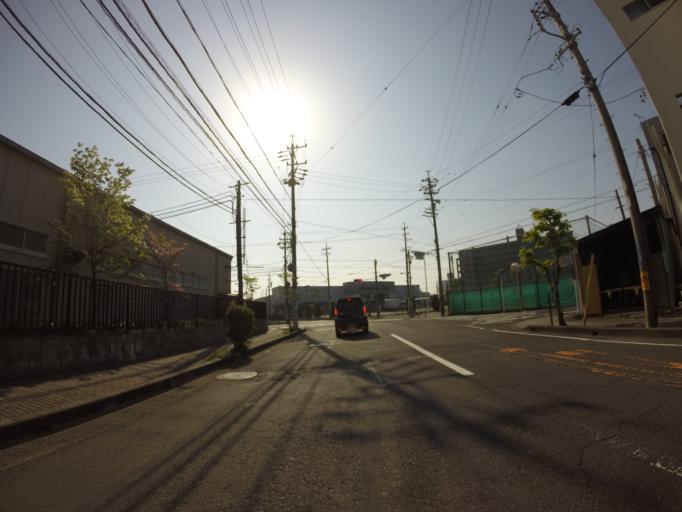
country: JP
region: Shizuoka
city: Shizuoka-shi
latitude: 35.0174
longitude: 138.4829
